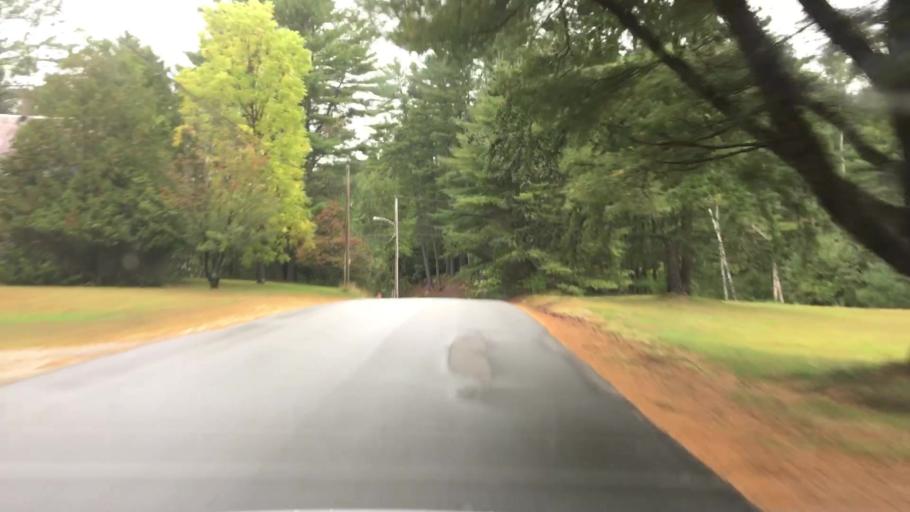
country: US
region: Maine
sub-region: Cumberland County
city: Raymond
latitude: 43.9983
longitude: -70.5689
